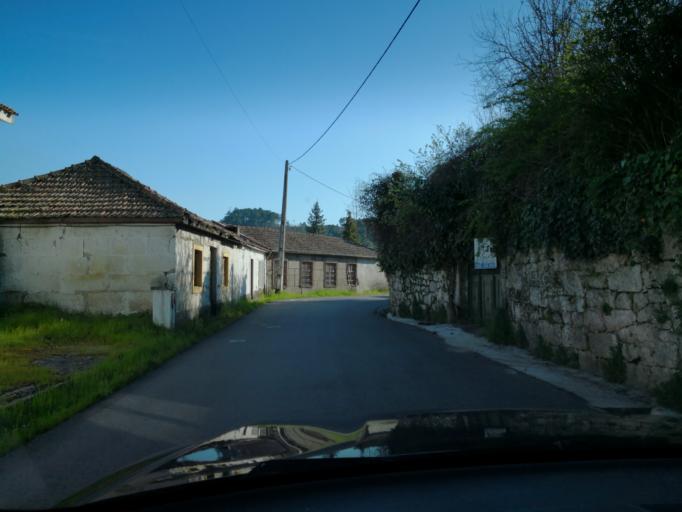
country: PT
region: Vila Real
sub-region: Vila Real
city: Vila Real
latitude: 41.2941
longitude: -7.7620
